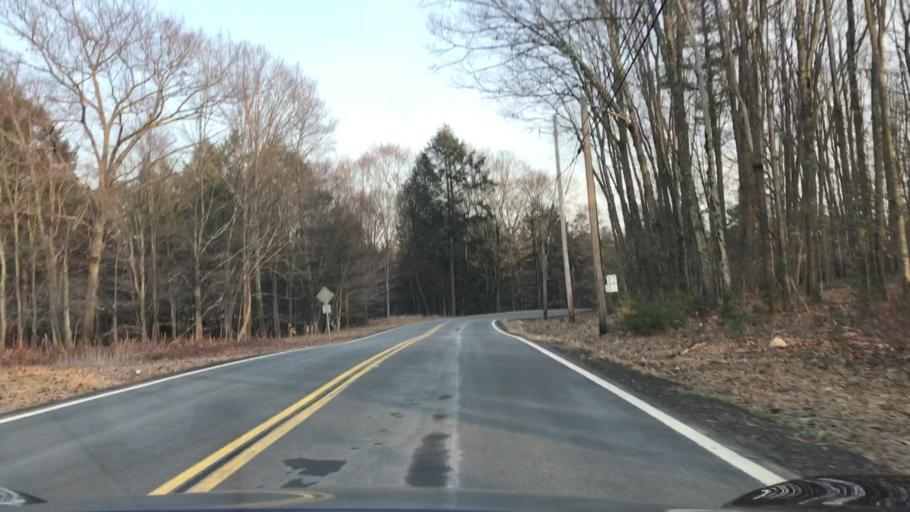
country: US
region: New York
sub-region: Sullivan County
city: Liberty
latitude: 41.6785
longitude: -74.9867
